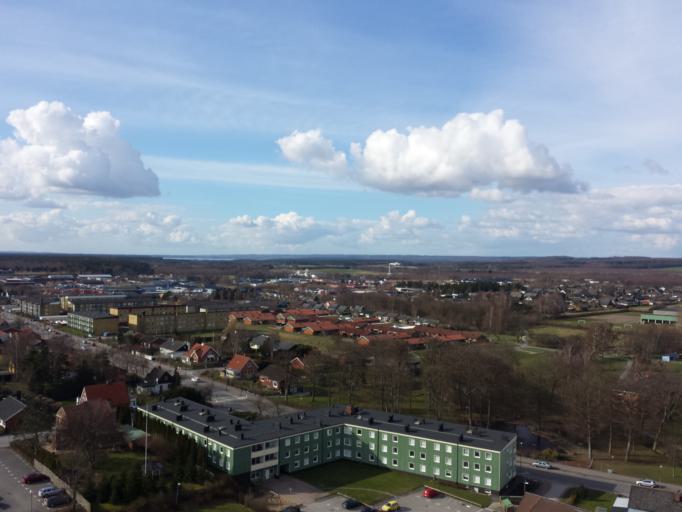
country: SE
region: Skane
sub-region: Sjobo Kommun
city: Sjoebo
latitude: 55.6322
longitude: 13.7025
